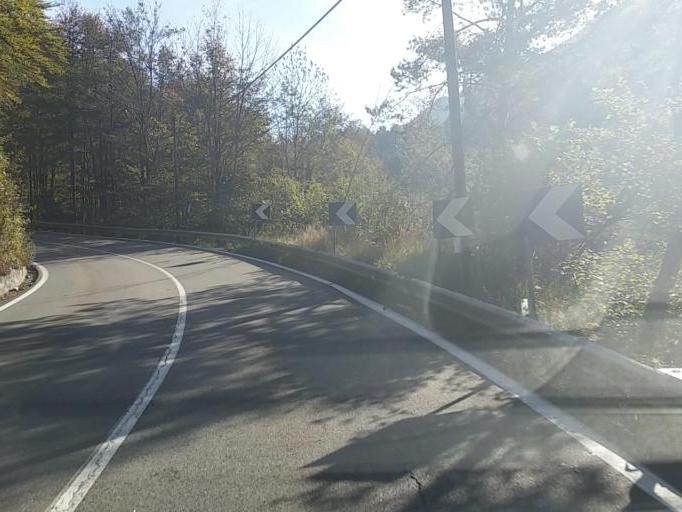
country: IT
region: Piedmont
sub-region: Provincia Verbano-Cusio-Ossola
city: Druogno
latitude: 46.1310
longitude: 8.4075
